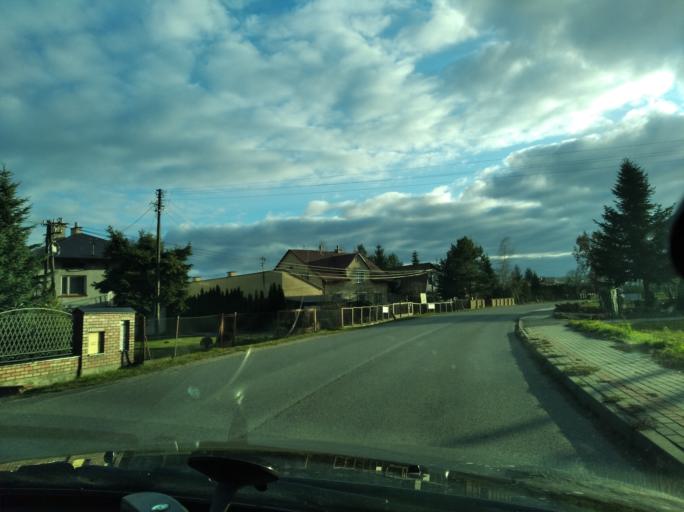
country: PL
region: Subcarpathian Voivodeship
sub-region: Powiat rzeszowski
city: Krasne
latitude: 50.0474
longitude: 22.1231
